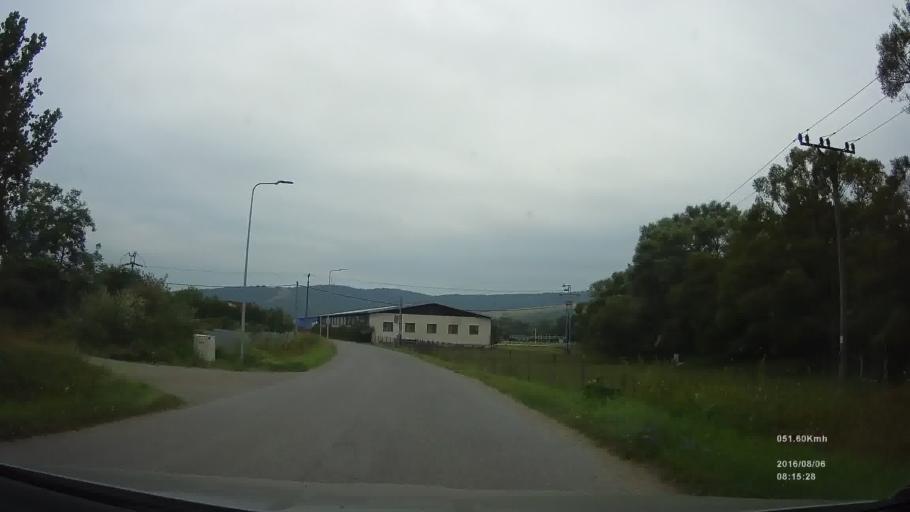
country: SK
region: Presovsky
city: Stropkov
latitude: 49.2141
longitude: 21.6515
